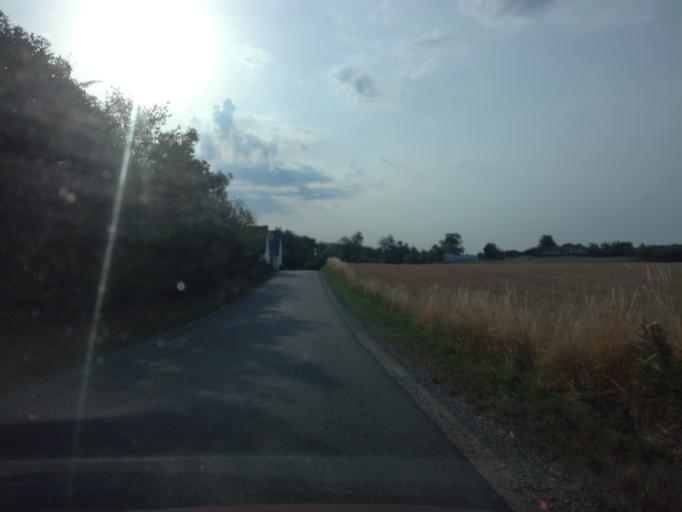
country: DK
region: South Denmark
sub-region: Vejle Kommune
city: Vejle
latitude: 55.6476
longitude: 9.5719
